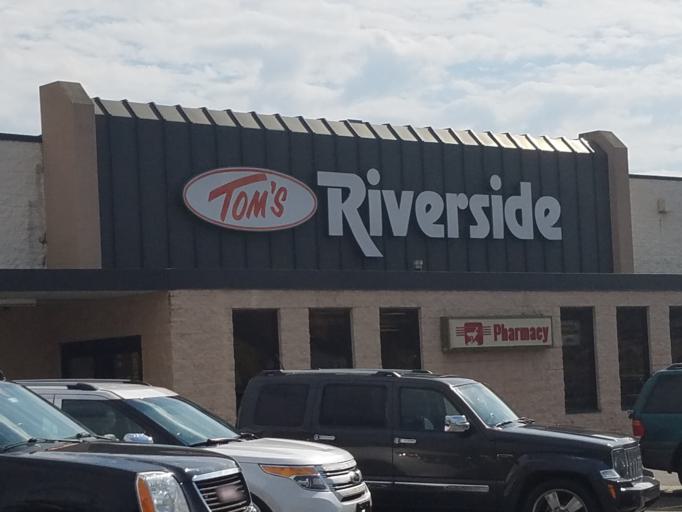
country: US
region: Pennsylvania
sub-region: Clarion County
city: Knox
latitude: 41.2300
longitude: -79.5284
